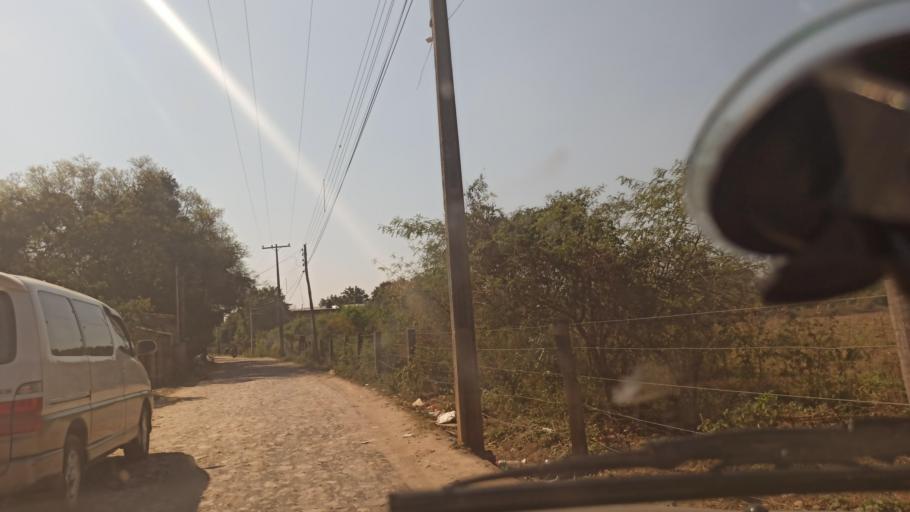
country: AR
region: Formosa
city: Clorinda
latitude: -25.2878
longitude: -57.6943
